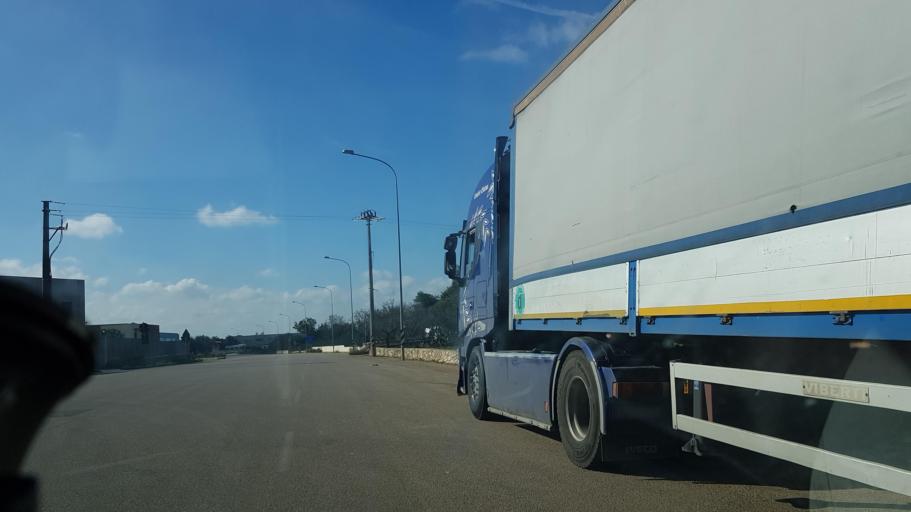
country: IT
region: Apulia
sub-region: Provincia di Brindisi
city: San Vito dei Normanni
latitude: 40.6714
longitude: 17.6991
